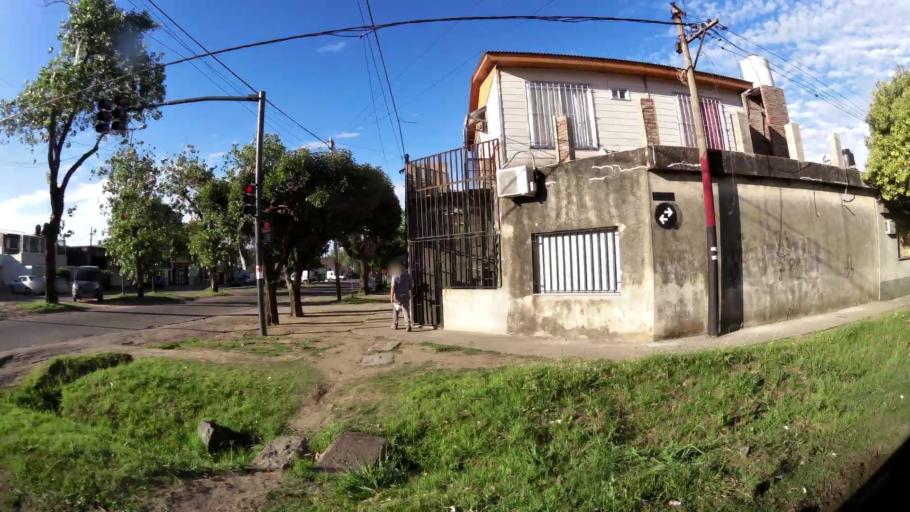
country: AR
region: Santa Fe
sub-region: Departamento de Rosario
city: Rosario
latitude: -32.9880
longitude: -60.6771
